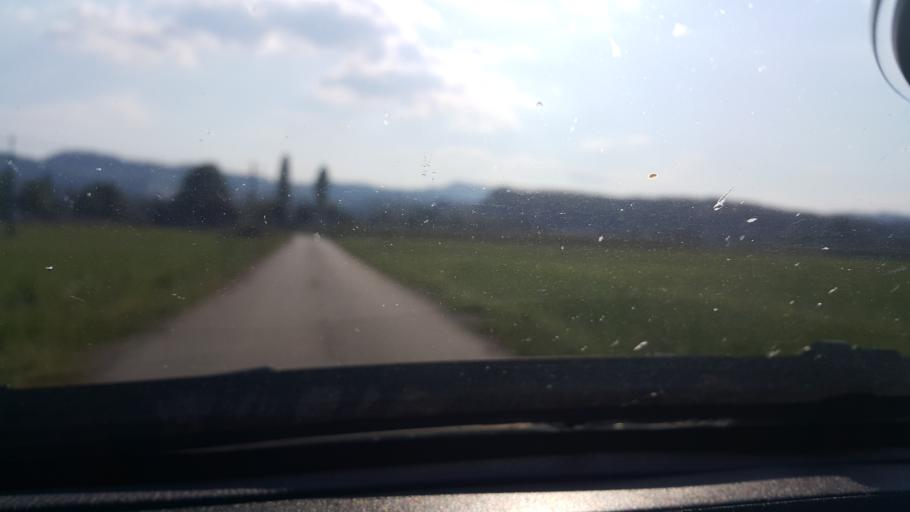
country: SI
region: Podcetrtek
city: Podcetrtek
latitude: 46.1023
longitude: 15.6207
